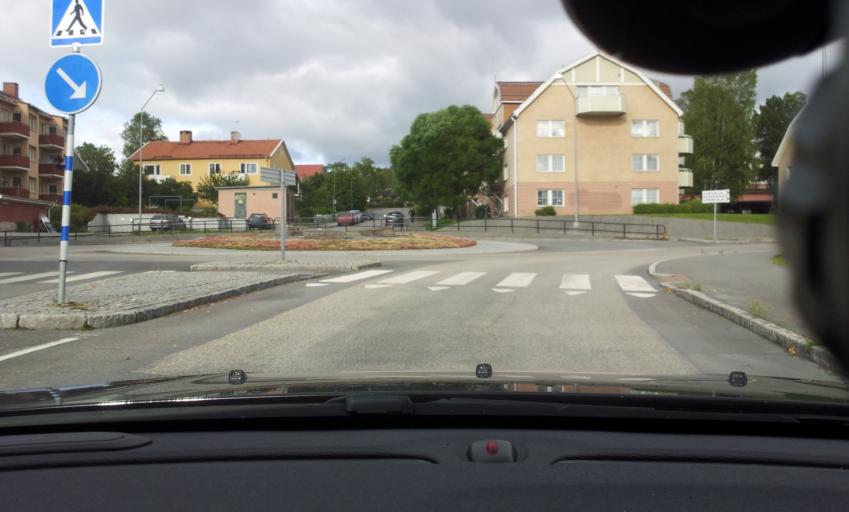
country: SE
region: Jaemtland
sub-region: OEstersunds Kommun
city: Ostersund
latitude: 63.1623
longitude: 14.6593
